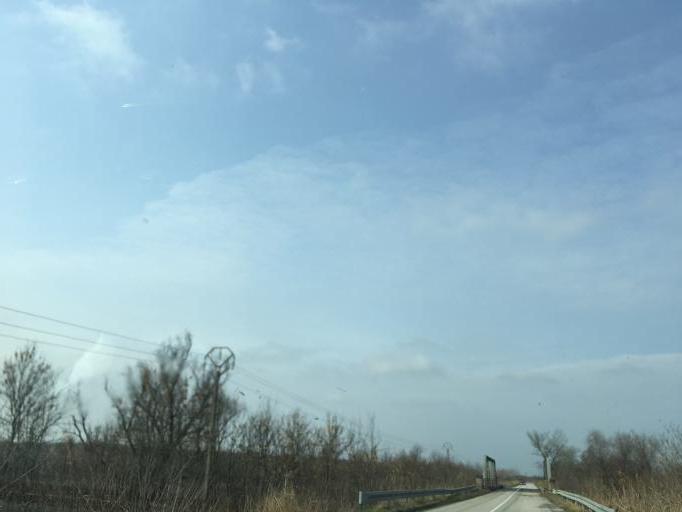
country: RS
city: Centa
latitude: 45.0954
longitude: 20.4143
